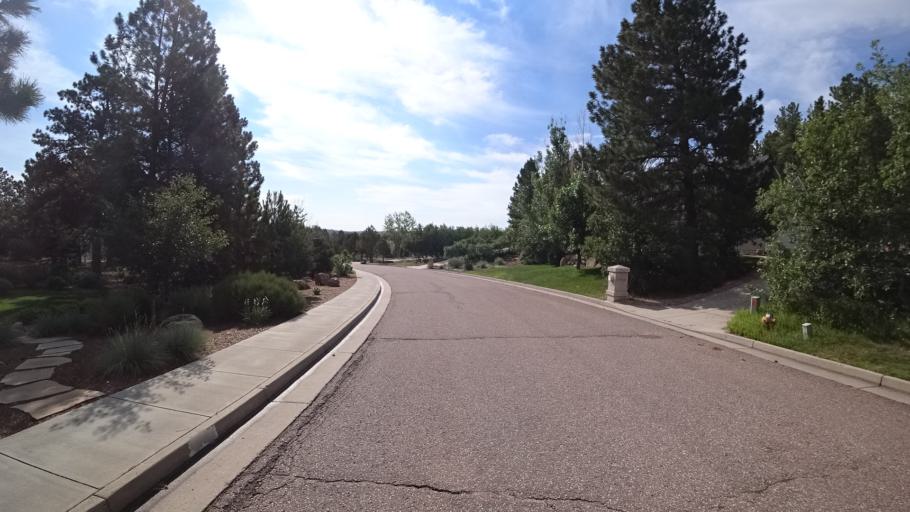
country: US
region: Colorado
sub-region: El Paso County
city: Air Force Academy
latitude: 38.9411
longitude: -104.8255
